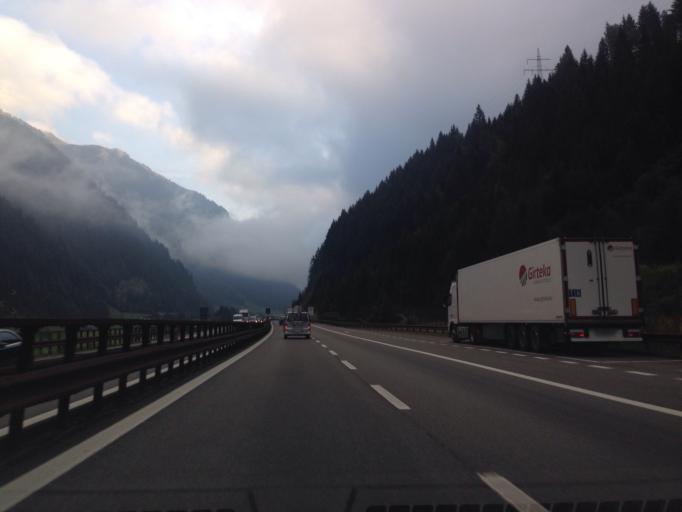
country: IT
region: Trentino-Alto Adige
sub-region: Bolzano
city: Colle Isarco
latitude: 46.9654
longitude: 11.4667
